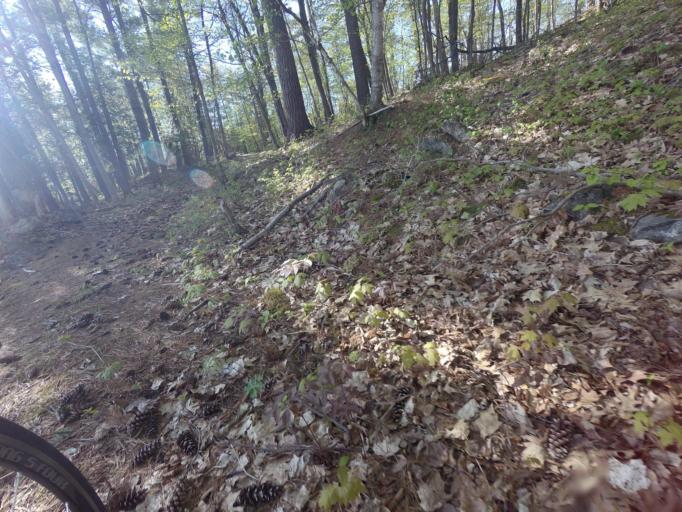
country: CA
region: Ontario
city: Arnprior
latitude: 45.4717
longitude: -76.3015
